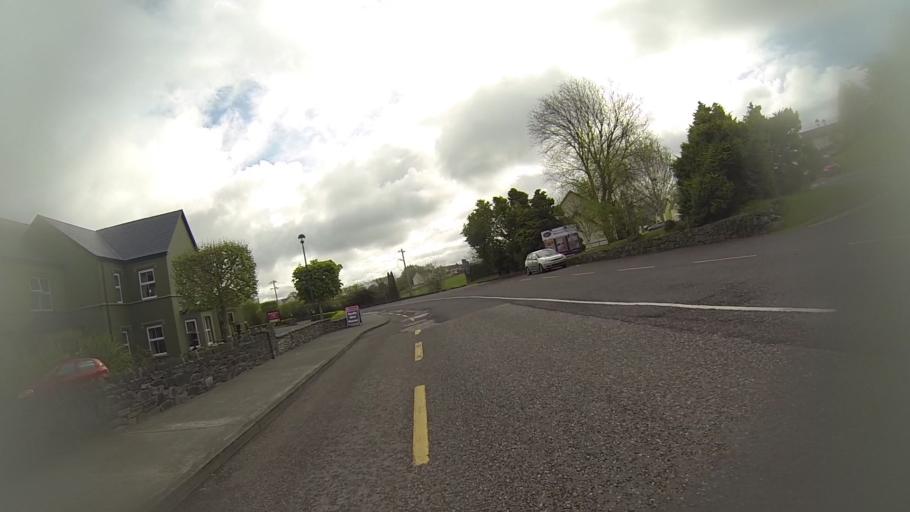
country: IE
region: Munster
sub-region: Ciarrai
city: Kenmare
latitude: 51.8832
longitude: -9.5919
